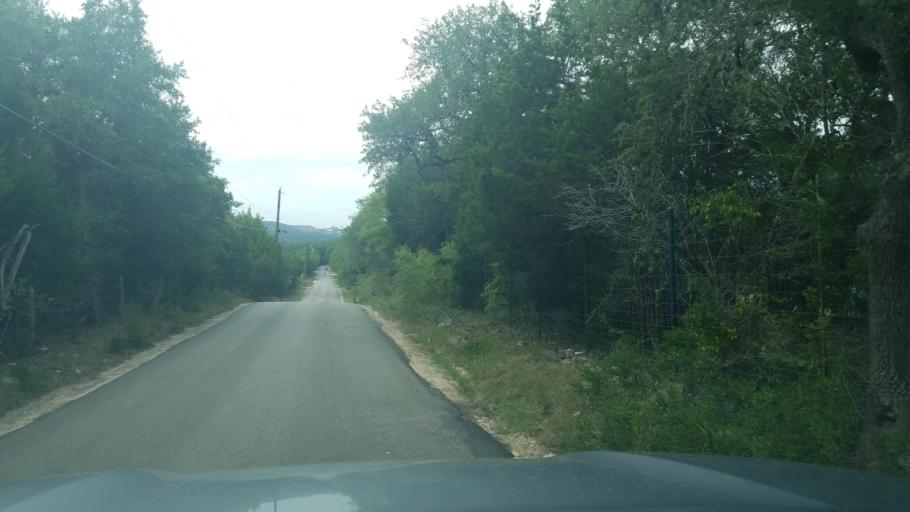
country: US
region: Texas
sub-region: Comal County
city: Bulverde
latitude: 29.7635
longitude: -98.4089
